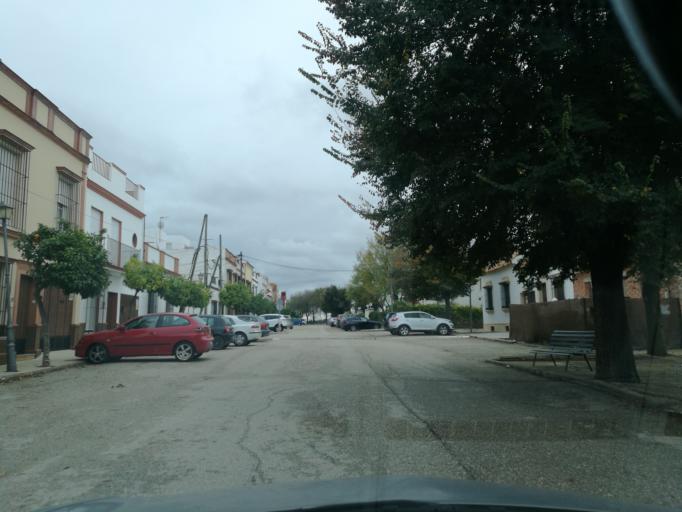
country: ES
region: Andalusia
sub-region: Provincia de Sevilla
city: La Campana
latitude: 37.5661
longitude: -5.4313
